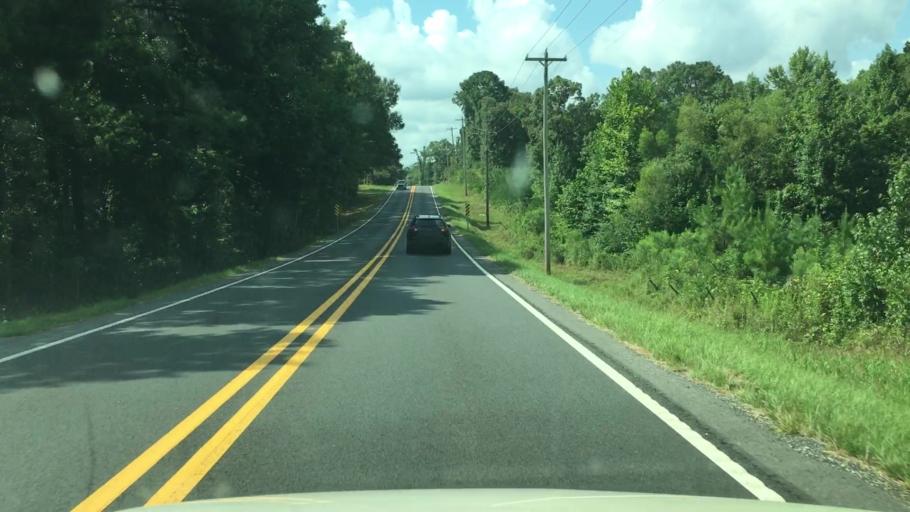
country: US
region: Arkansas
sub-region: Garland County
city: Lake Hamilton
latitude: 34.2886
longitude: -93.1635
